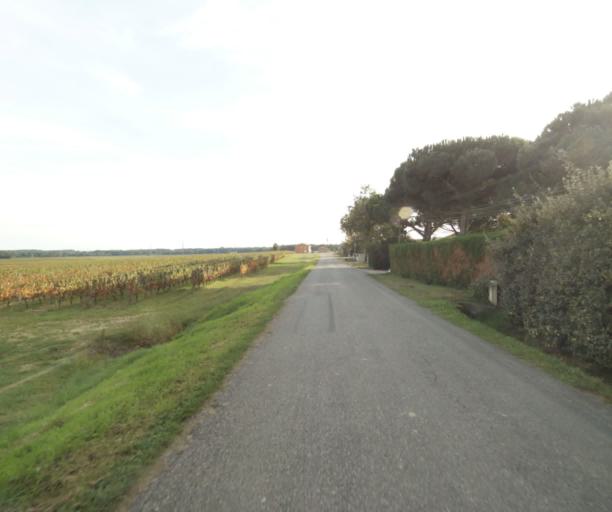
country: FR
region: Midi-Pyrenees
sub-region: Departement du Tarn-et-Garonne
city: Campsas
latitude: 43.8879
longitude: 1.3255
